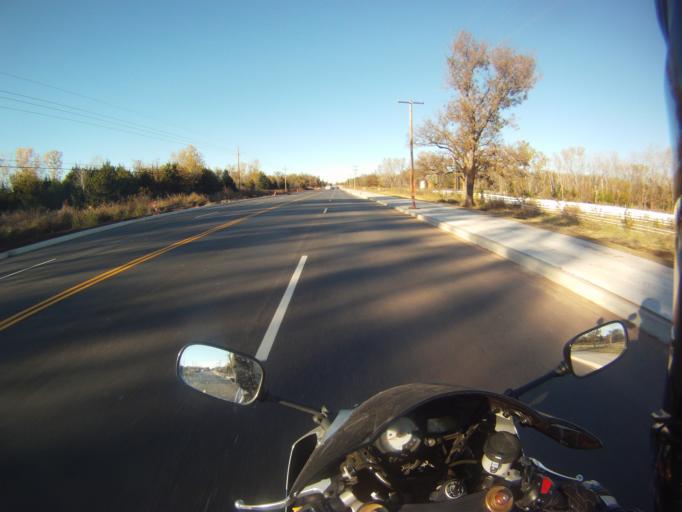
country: US
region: Oklahoma
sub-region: Payne County
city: Stillwater
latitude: 36.1198
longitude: -97.1229
